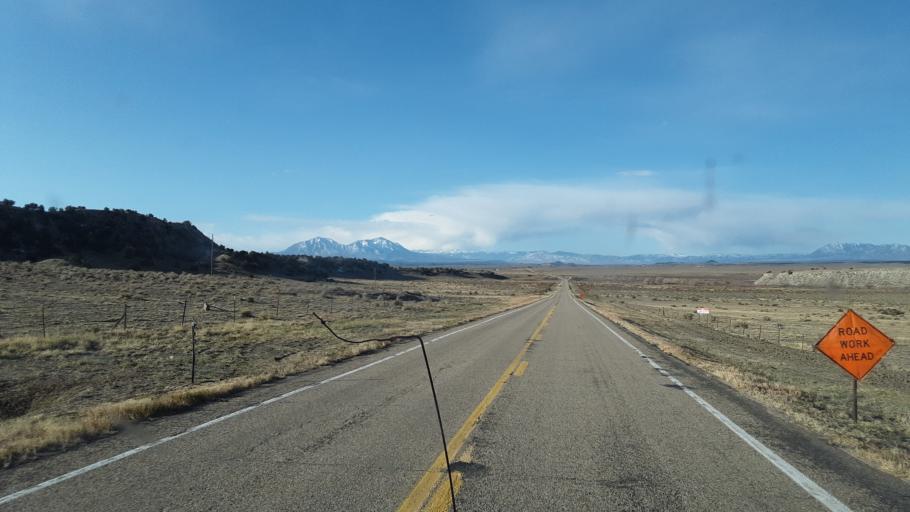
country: US
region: Colorado
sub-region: Huerfano County
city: Walsenburg
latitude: 37.6898
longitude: -104.6361
